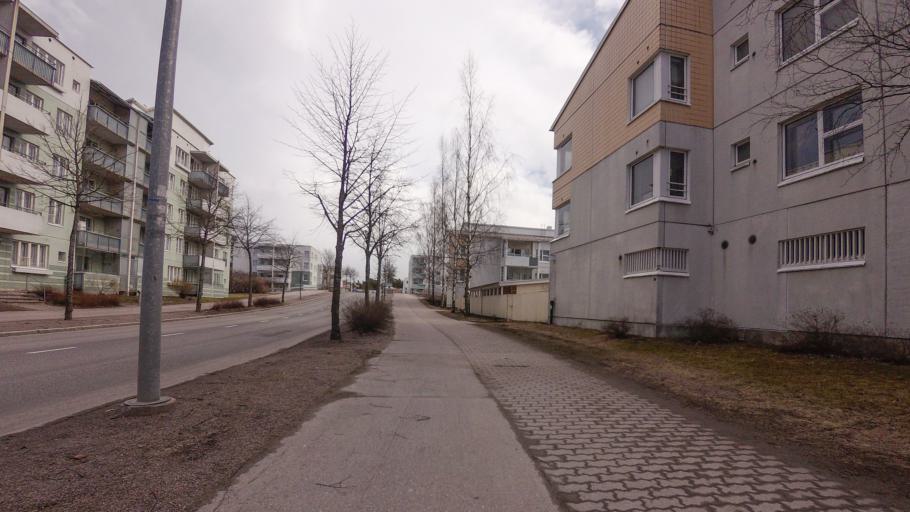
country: FI
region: Uusimaa
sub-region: Helsinki
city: Vantaa
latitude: 60.2009
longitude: 25.1174
